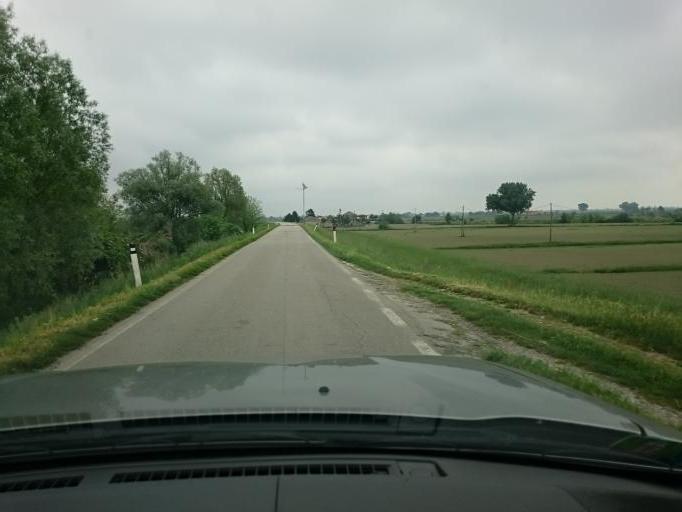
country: IT
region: Veneto
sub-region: Provincia di Padova
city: Pontelongo
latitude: 45.2440
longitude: 12.0417
